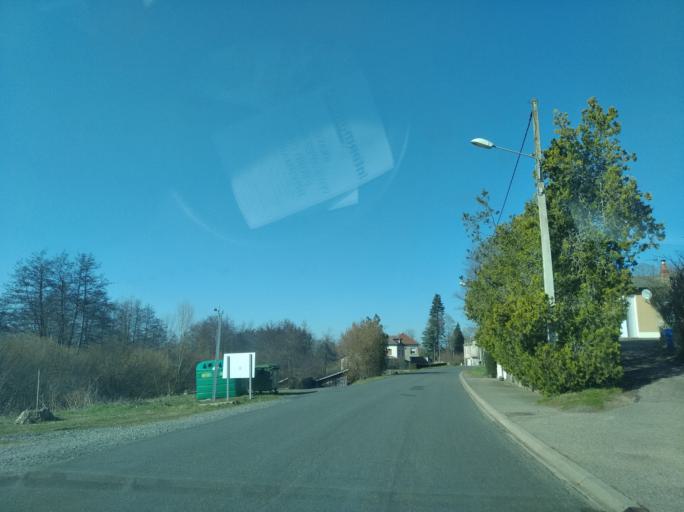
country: FR
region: Auvergne
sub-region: Departement de l'Allier
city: Le Mayet-de-Montagne
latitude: 46.0644
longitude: 3.6690
